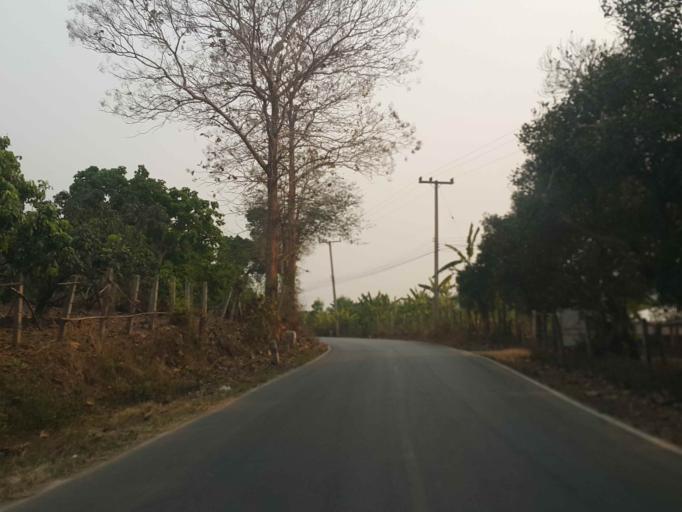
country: TH
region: Chiang Mai
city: Mae Taeng
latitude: 19.1040
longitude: 98.8989
